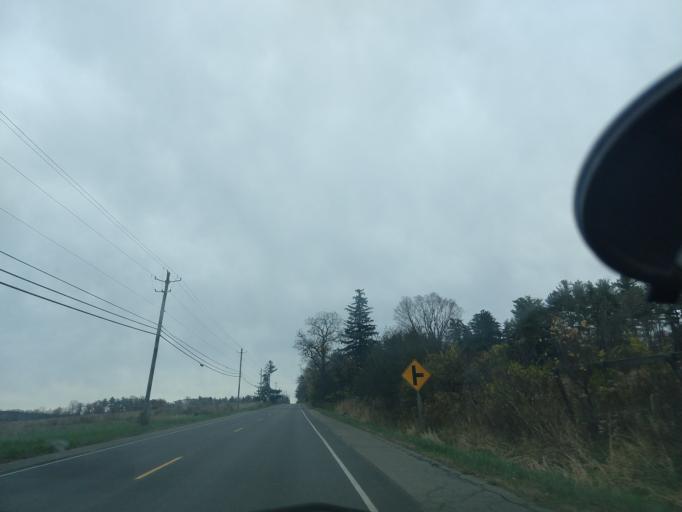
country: US
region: New York
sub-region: Tompkins County
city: East Ithaca
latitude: 42.4347
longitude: -76.4567
